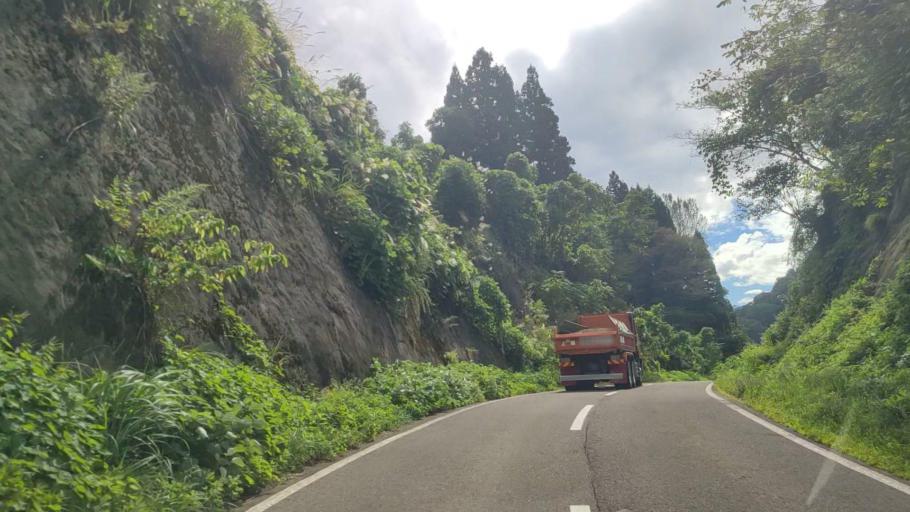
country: JP
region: Niigata
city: Arai
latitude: 36.9386
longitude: 138.2932
